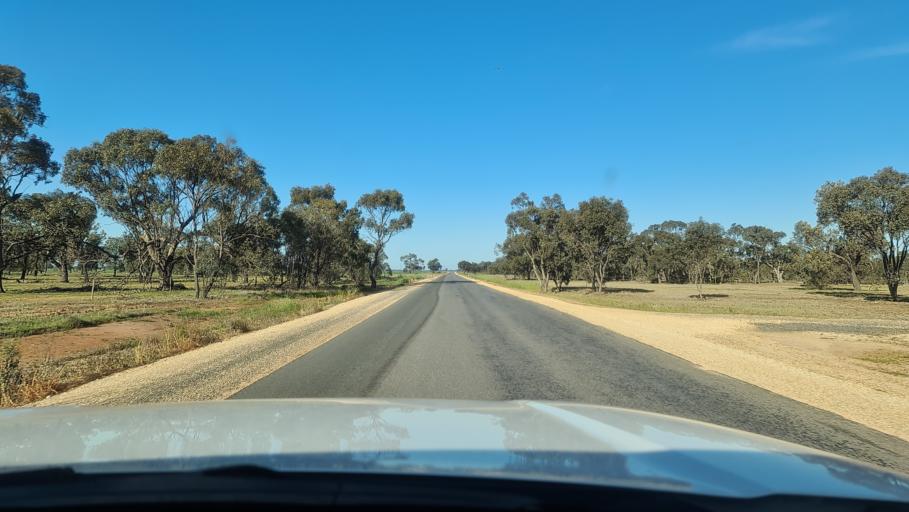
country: AU
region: Victoria
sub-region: Horsham
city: Horsham
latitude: -36.4492
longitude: 142.5363
